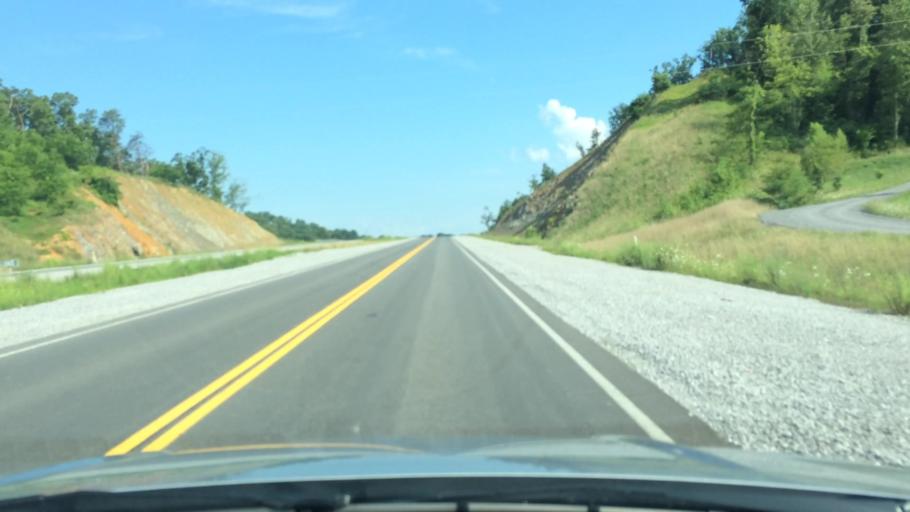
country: US
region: Tennessee
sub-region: Jefferson County
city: White Pine
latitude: 36.1350
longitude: -83.3373
